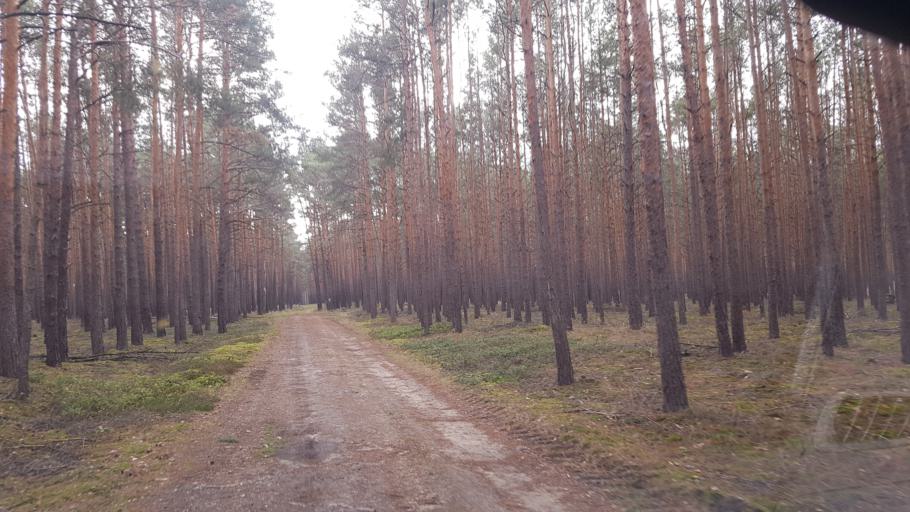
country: DE
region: Brandenburg
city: Schonborn
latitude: 51.6580
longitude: 13.4709
